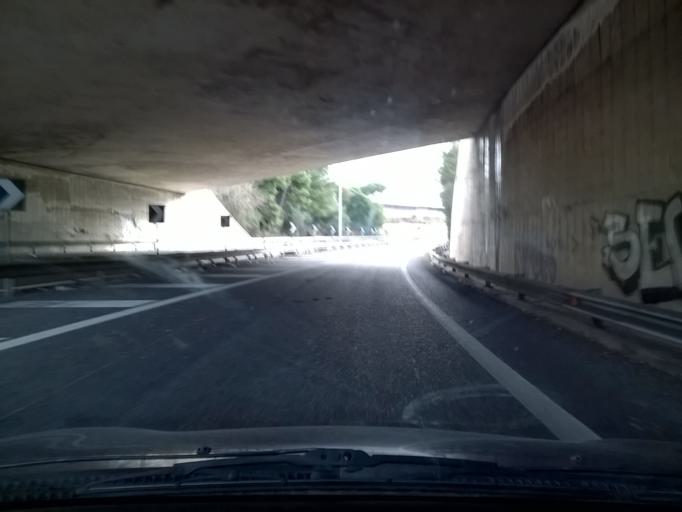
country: IT
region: Apulia
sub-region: Provincia di Taranto
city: Paolo VI
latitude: 40.4653
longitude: 17.2884
